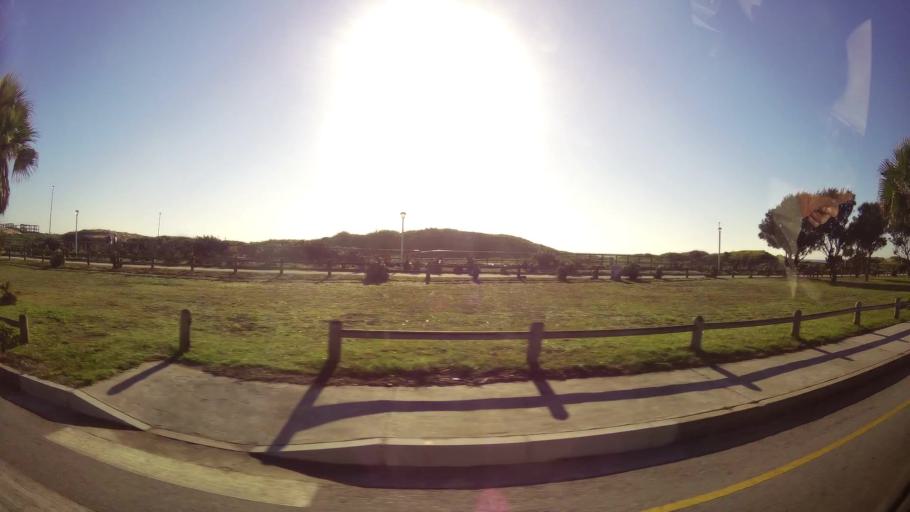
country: ZA
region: Eastern Cape
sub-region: Nelson Mandela Bay Metropolitan Municipality
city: Port Elizabeth
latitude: -33.9903
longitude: 25.6745
